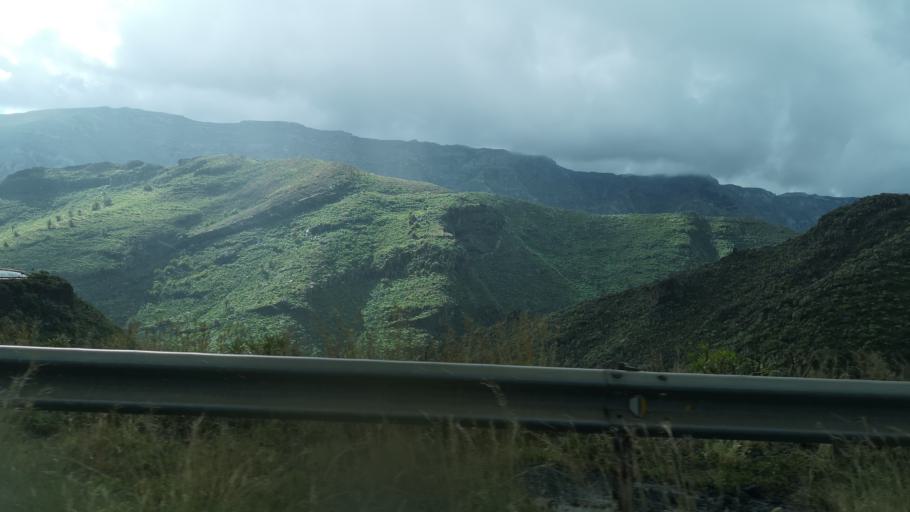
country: ES
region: Canary Islands
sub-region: Provincia de Santa Cruz de Tenerife
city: San Sebastian de la Gomera
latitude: 28.1235
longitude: -17.1460
